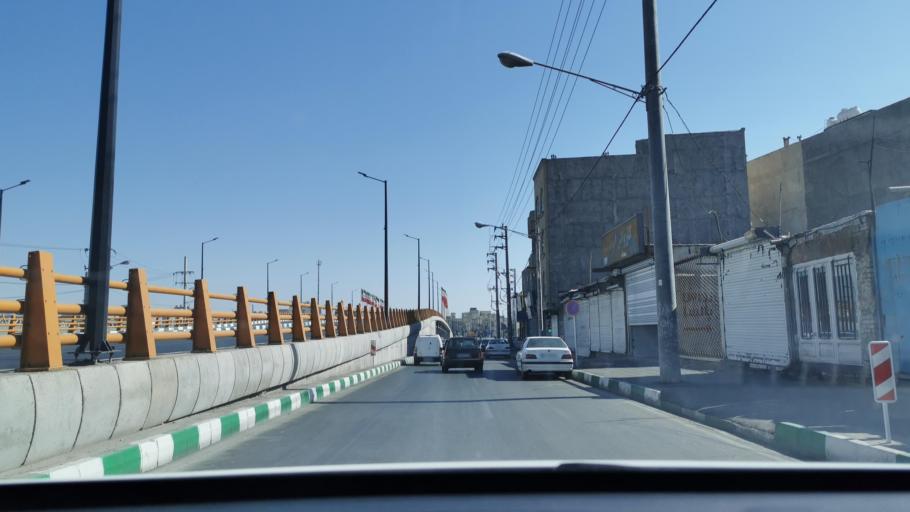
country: IR
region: Razavi Khorasan
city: Mashhad
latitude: 36.3350
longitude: 59.6041
